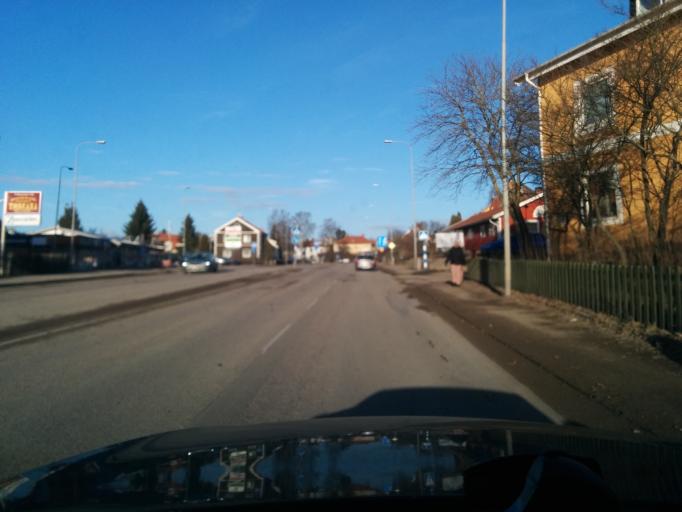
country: SE
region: Vaestmanland
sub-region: Vasteras
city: Vasteras
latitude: 59.6207
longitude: 16.5725
